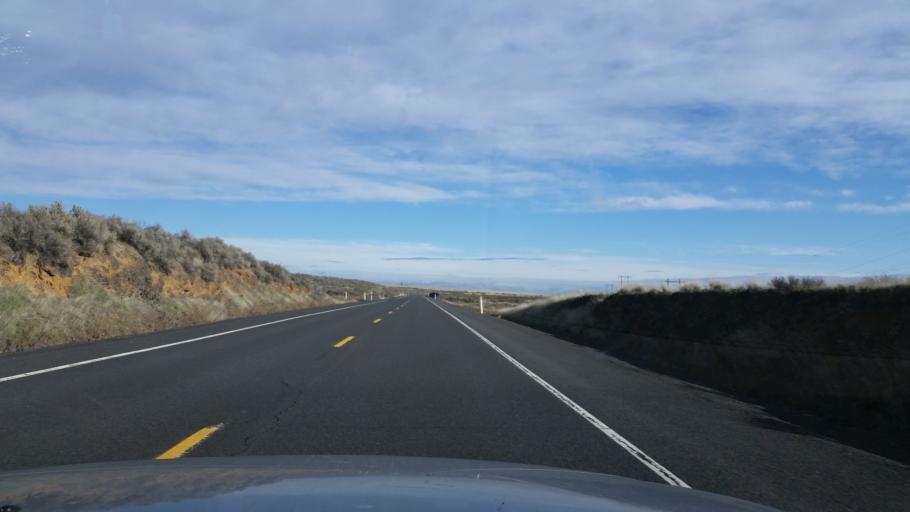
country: US
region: Washington
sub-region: Adams County
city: Ritzville
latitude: 47.3656
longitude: -118.4634
